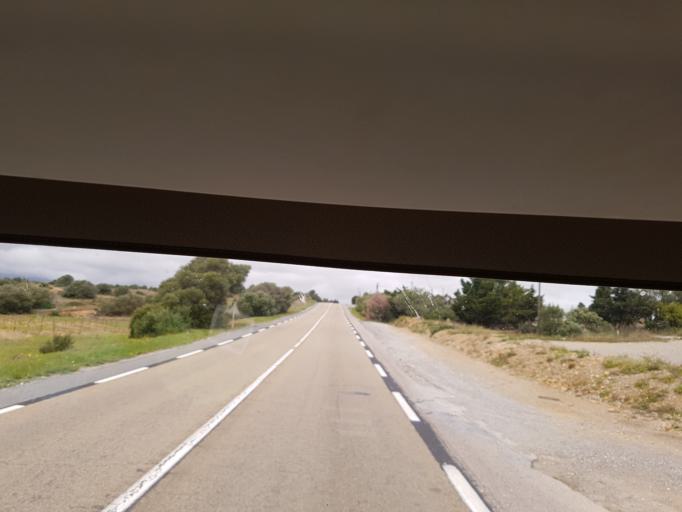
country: FR
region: Languedoc-Roussillon
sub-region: Departement de l'Aude
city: Leucate
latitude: 42.9036
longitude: 3.0010
